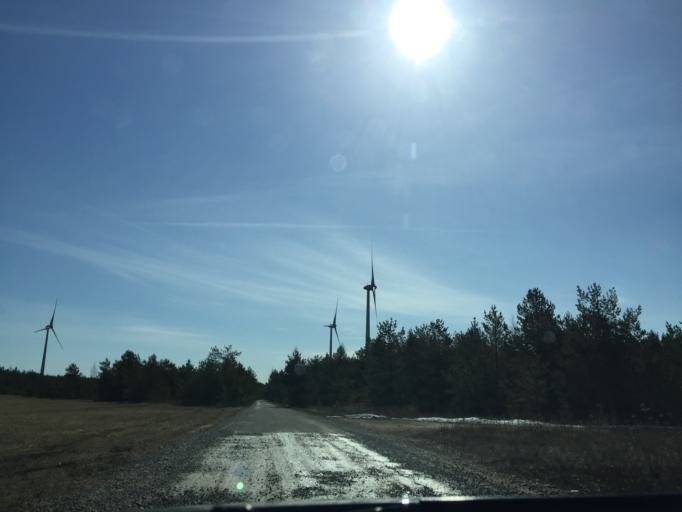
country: EE
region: Laeaene
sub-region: Lihula vald
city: Lihula
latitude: 58.6225
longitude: 23.5447
